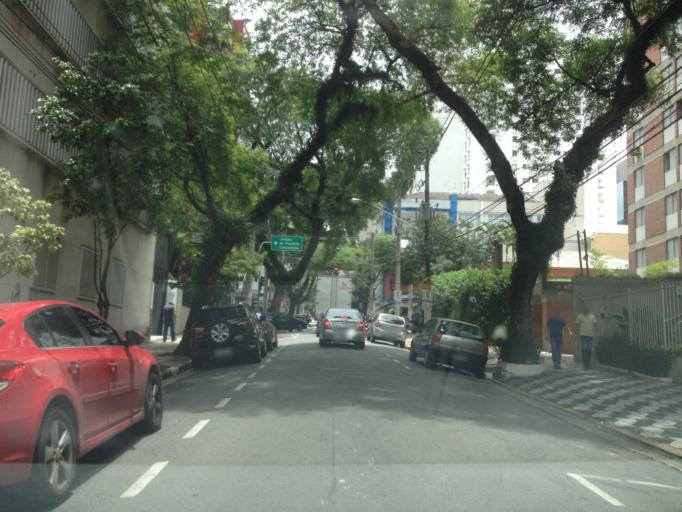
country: BR
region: Sao Paulo
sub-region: Sao Paulo
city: Sao Paulo
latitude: -23.5710
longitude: -46.6508
